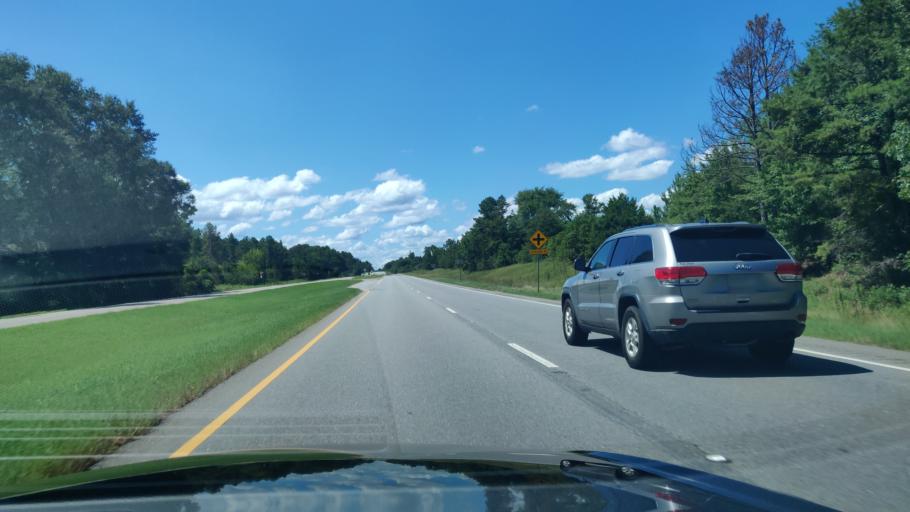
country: US
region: Georgia
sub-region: Terrell County
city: Dawson
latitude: 31.8830
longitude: -84.5032
